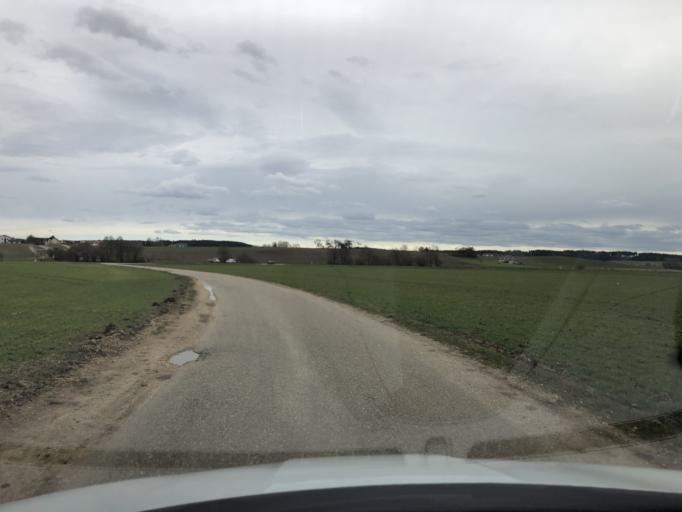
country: DE
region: Baden-Wuerttemberg
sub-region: Tuebingen Region
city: Dettingen
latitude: 48.2367
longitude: 9.7227
